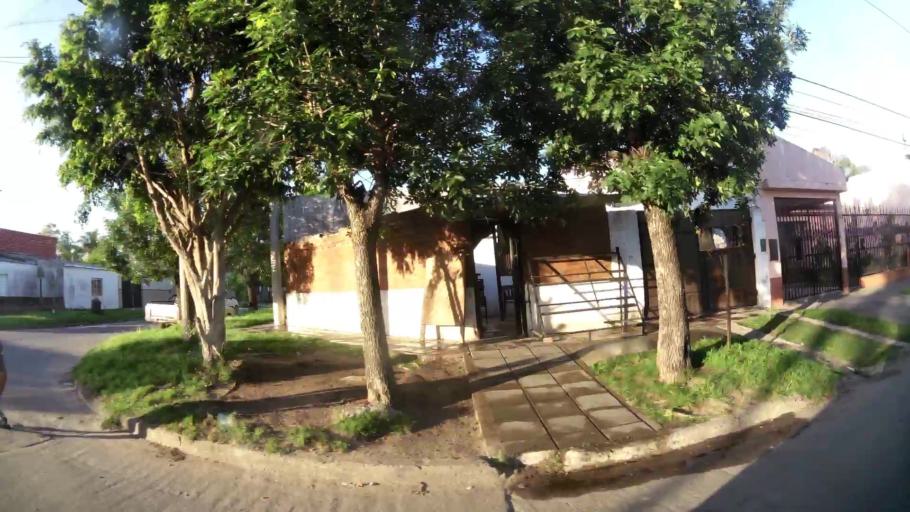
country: AR
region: Santa Fe
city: Santa Fe de la Vera Cruz
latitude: -31.6002
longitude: -60.6834
